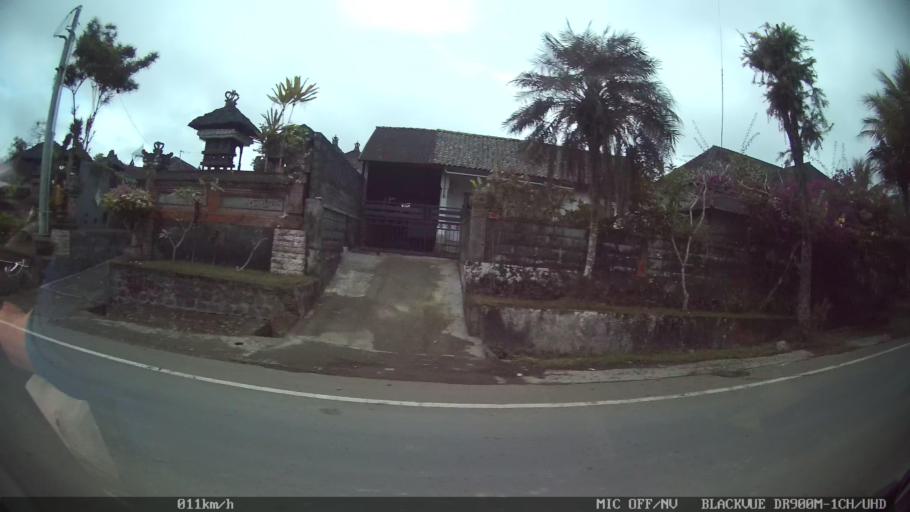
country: ID
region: Bali
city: Banjar Geriana Kangin
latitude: -8.3817
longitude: 115.4447
